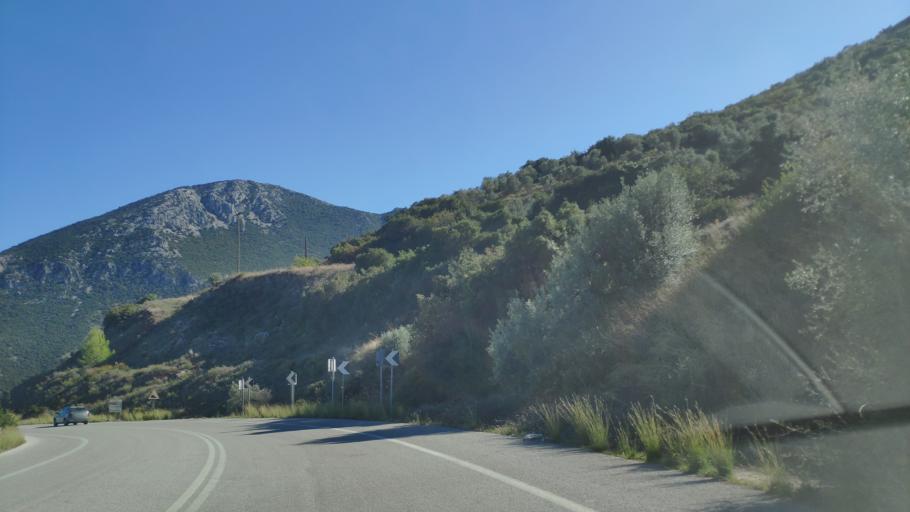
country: GR
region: Peloponnese
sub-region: Nomos Argolidos
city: Palaia Epidavros
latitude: 37.6112
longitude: 23.1523
